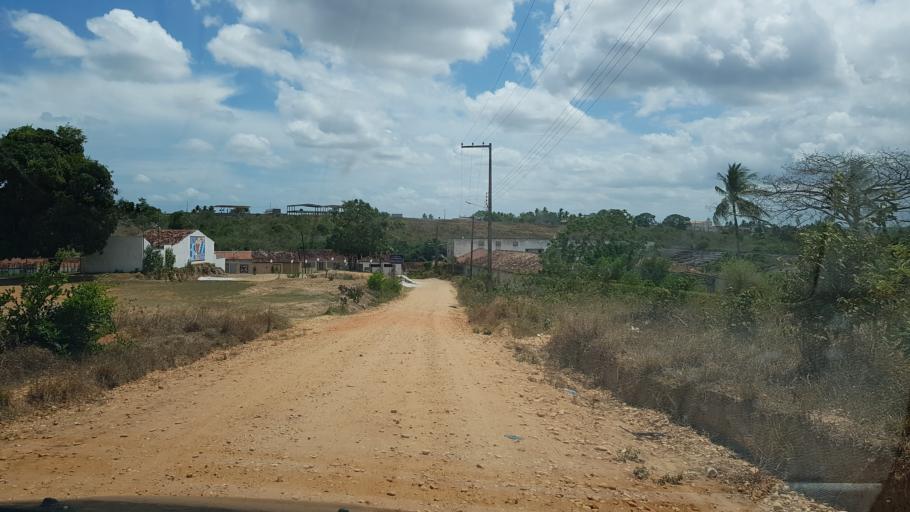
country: BR
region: Alagoas
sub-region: Penedo
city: Penedo
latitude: -10.2863
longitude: -36.5704
